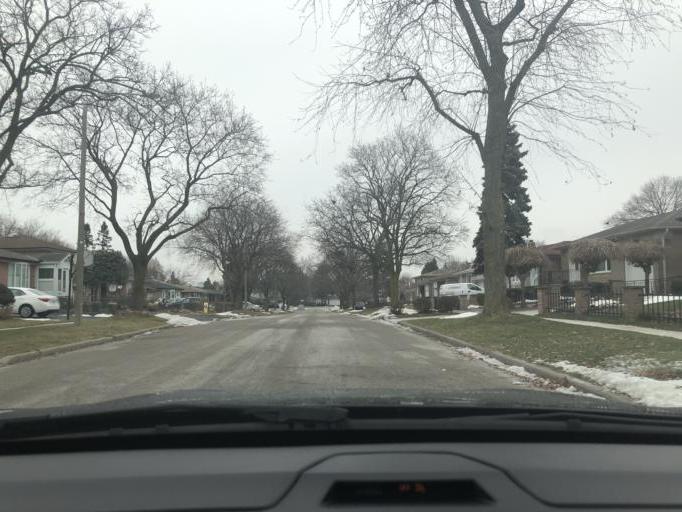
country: CA
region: Ontario
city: Scarborough
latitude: 43.7834
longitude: -79.2749
